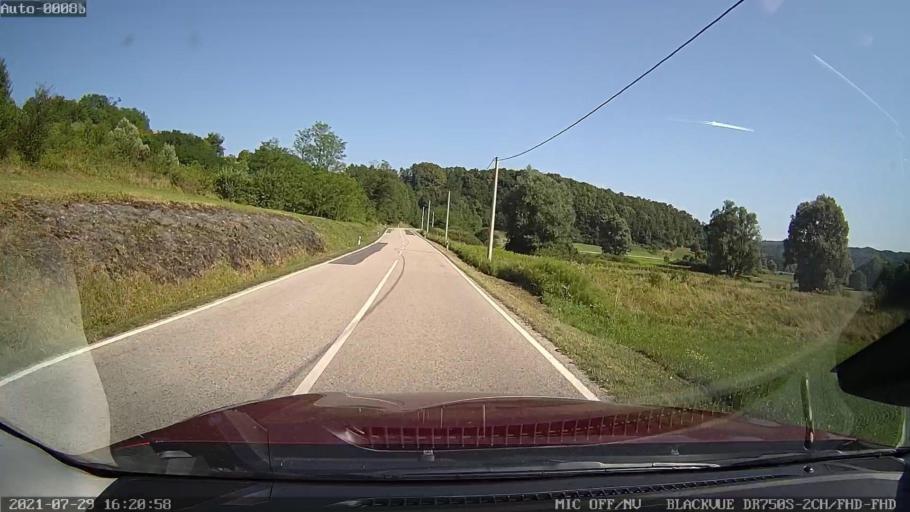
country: HR
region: Varazdinska
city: Lepoglava
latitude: 46.2371
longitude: 15.9645
